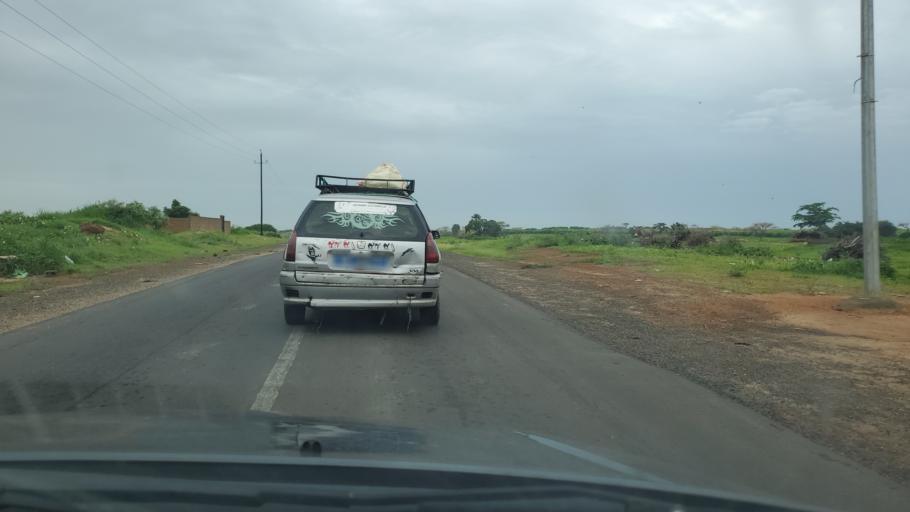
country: SN
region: Thies
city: Mekhe
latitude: 15.1584
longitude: -16.8266
